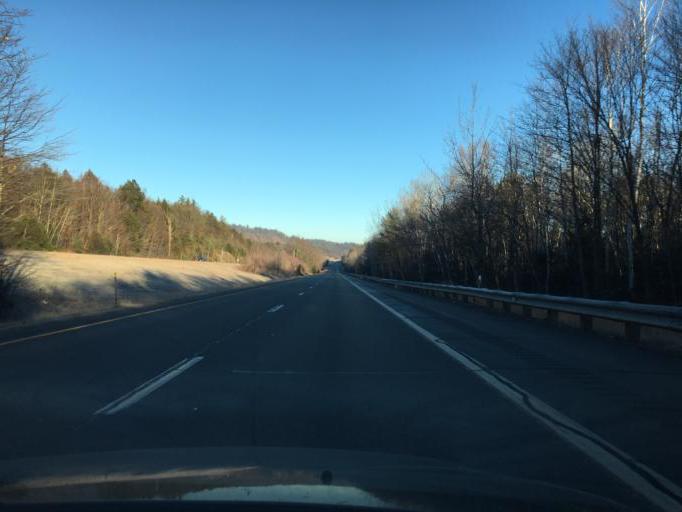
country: US
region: New Hampshire
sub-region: Belknap County
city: Sanbornton
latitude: 43.5625
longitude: -71.6176
